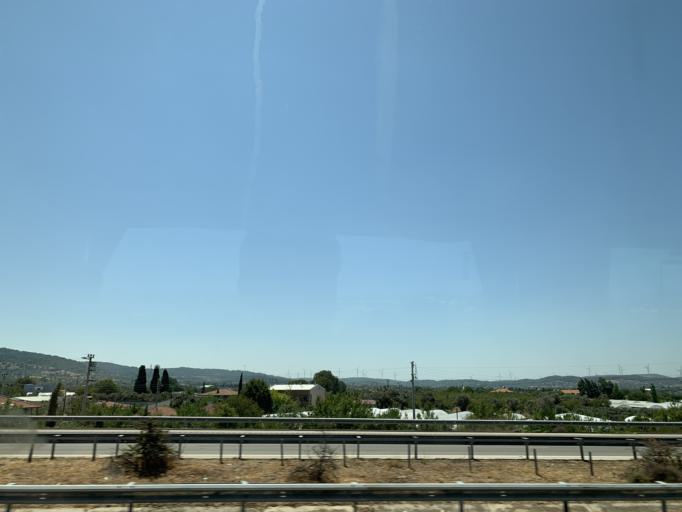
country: TR
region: Izmir
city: Urla
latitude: 38.2999
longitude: 26.7420
